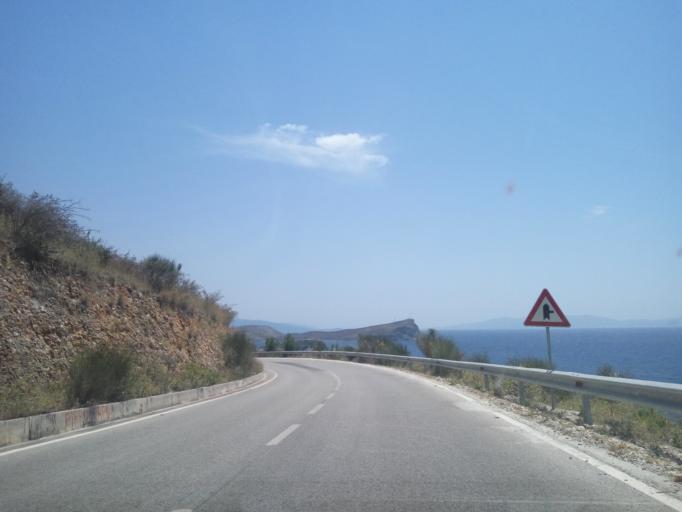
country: AL
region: Vlore
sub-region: Rrethi i Vlores
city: Himare
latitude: 40.0744
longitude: 19.7797
